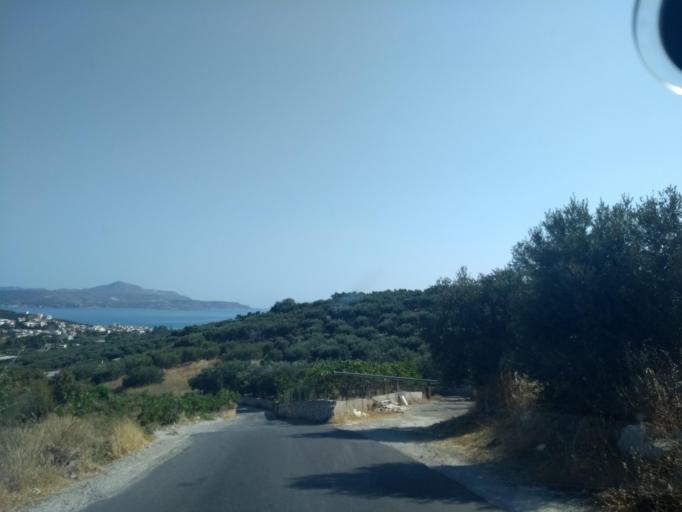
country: GR
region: Crete
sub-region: Nomos Chanias
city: Kalivai
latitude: 35.4394
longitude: 24.1722
